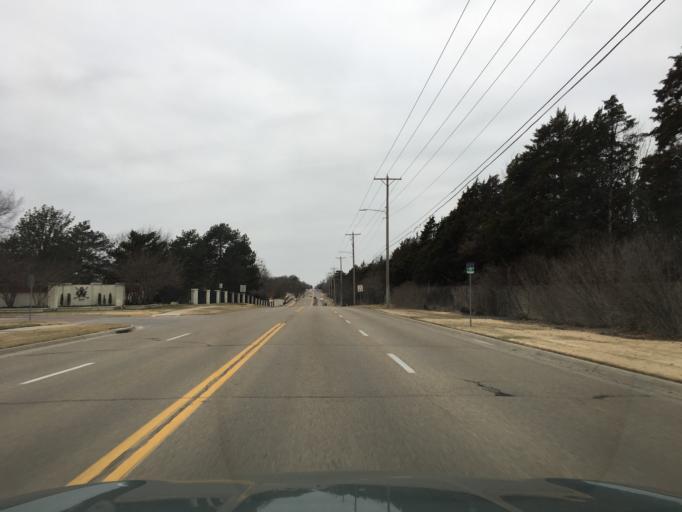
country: US
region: Kansas
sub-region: Sedgwick County
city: Bellaire
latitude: 37.7084
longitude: -97.2357
